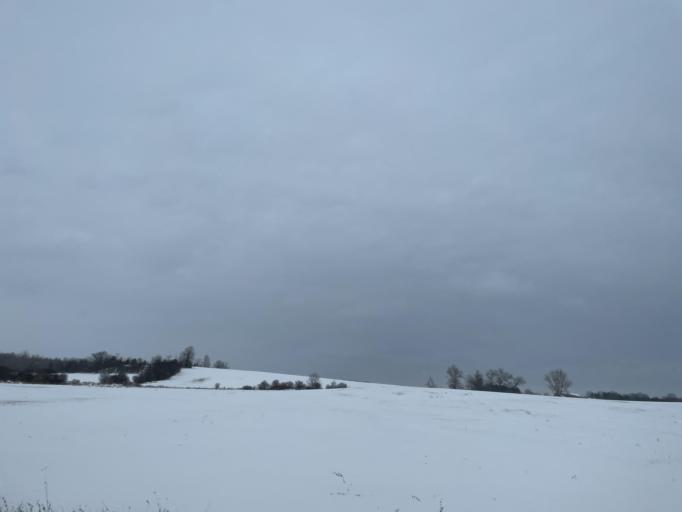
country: CA
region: Ontario
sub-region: Wellington County
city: Guelph
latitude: 43.5082
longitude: -80.3469
